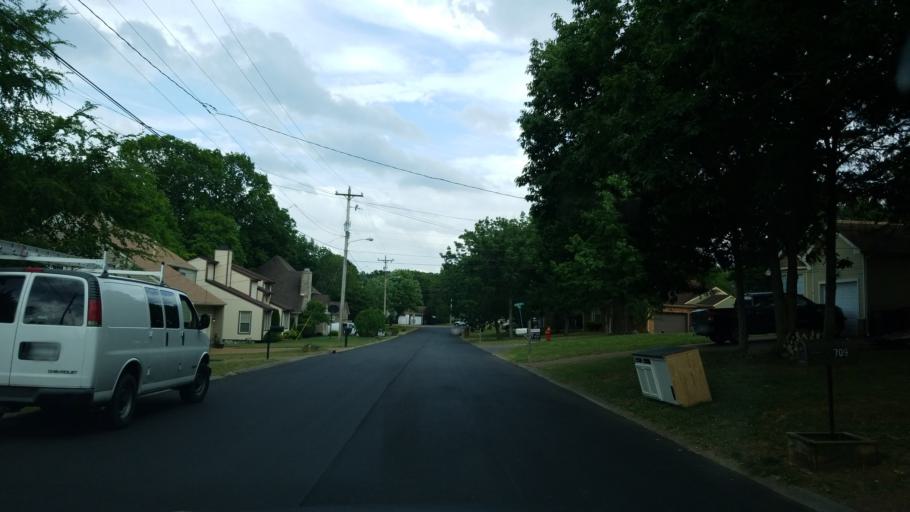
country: US
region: Tennessee
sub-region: Rutherford County
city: La Vergne
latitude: 36.0798
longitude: -86.6147
